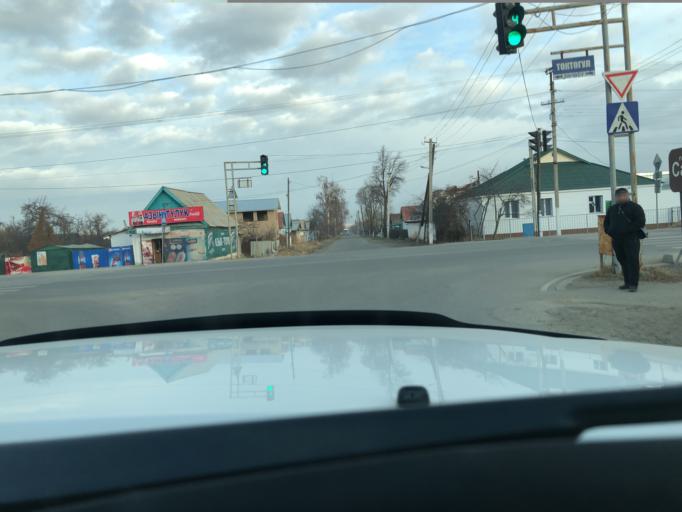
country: KG
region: Ysyk-Koel
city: Karakol
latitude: 42.4830
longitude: 78.3704
